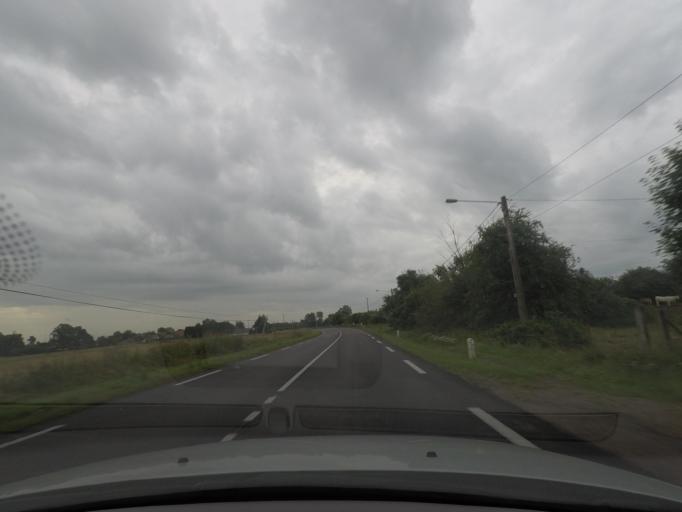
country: FR
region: Haute-Normandie
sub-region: Departement de la Seine-Maritime
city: Neufchatel-en-Bray
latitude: 49.7331
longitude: 1.5067
